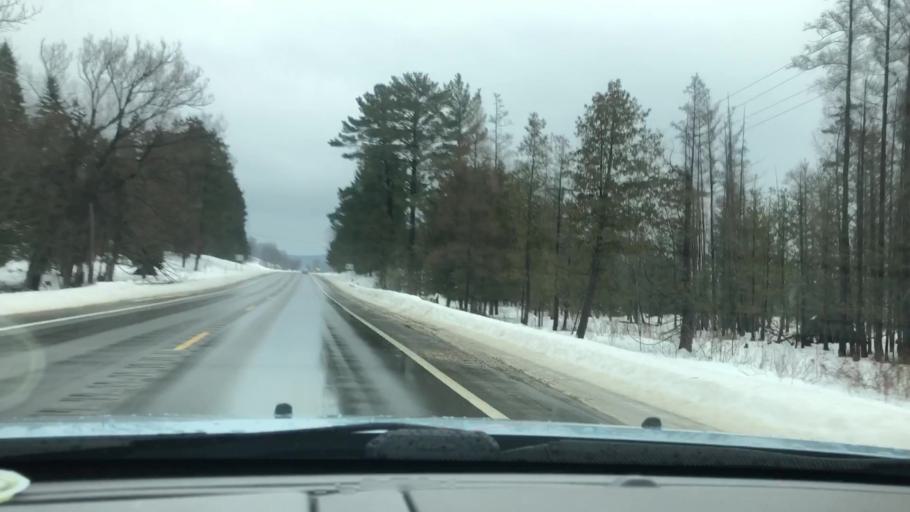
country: US
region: Michigan
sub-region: Charlevoix County
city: Boyne City
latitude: 45.0944
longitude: -84.9620
